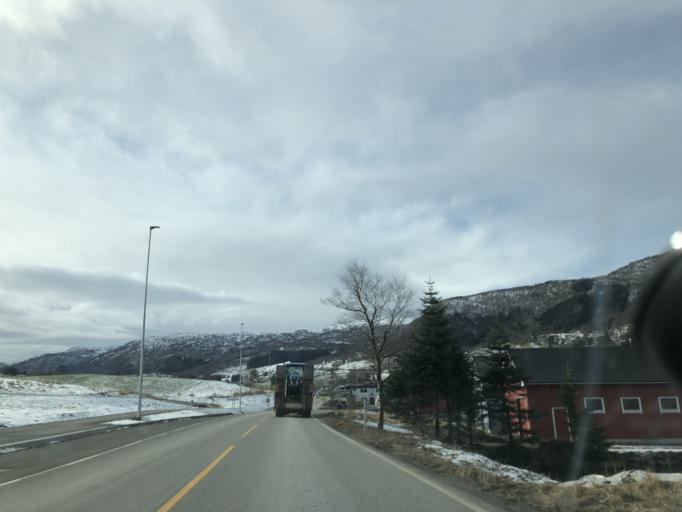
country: NO
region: Rogaland
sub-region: Vindafjord
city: Olen
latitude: 59.6000
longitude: 5.7585
